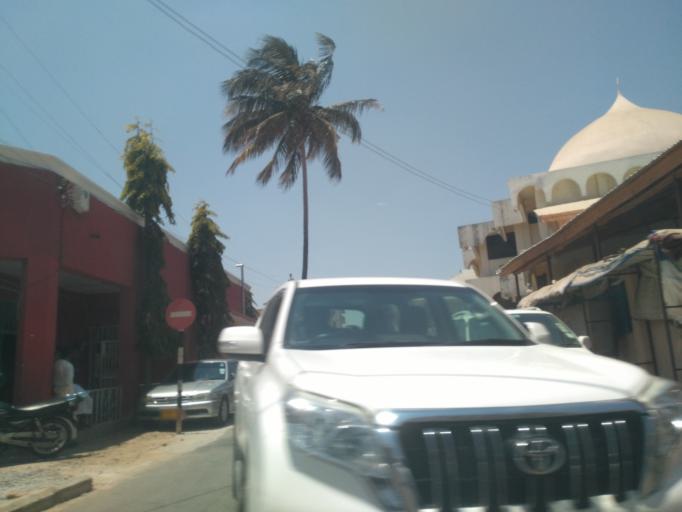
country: TZ
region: Dodoma
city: Dodoma
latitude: -6.1796
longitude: 35.7458
